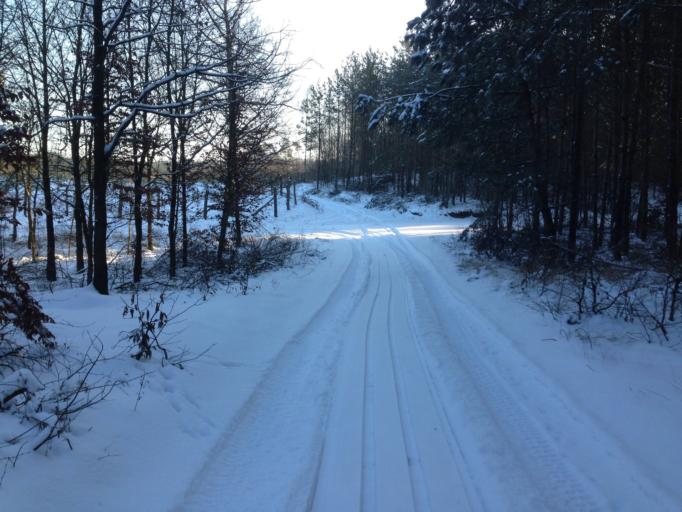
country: PL
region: Kujawsko-Pomorskie
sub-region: Powiat brodnicki
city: Gorzno
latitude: 53.1864
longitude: 19.6820
